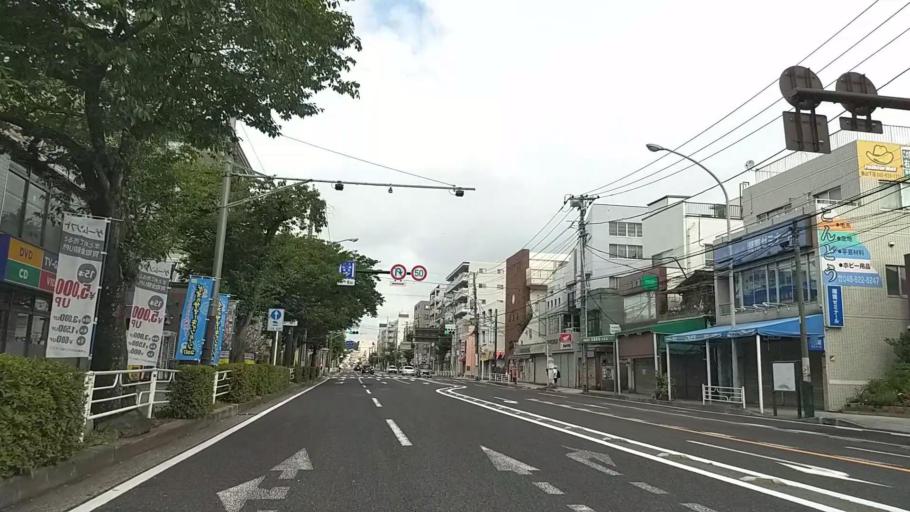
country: JP
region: Kanagawa
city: Yokohama
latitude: 35.4293
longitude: 139.6635
